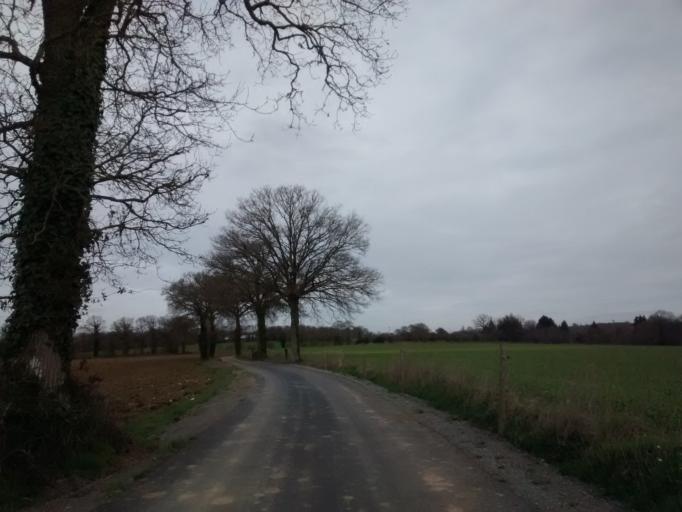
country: FR
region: Brittany
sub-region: Departement d'Ille-et-Vilaine
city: Liffre
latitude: 48.2101
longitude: -1.4763
